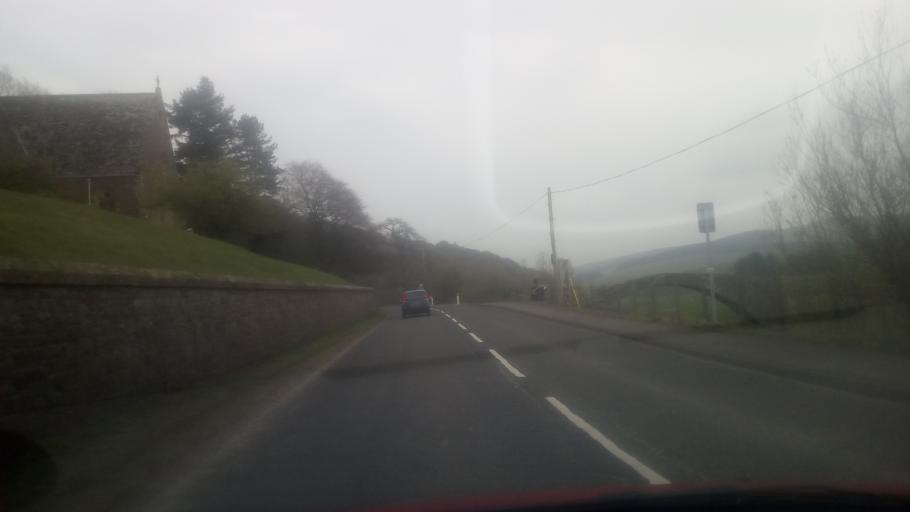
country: GB
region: Scotland
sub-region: The Scottish Borders
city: Galashiels
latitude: 55.6904
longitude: -2.8623
